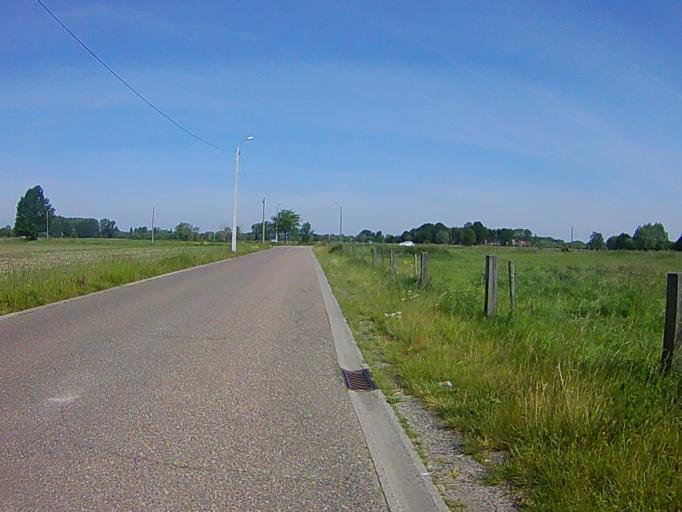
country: BE
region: Flanders
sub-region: Provincie Vlaams-Brabant
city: Londerzeel
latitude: 51.0289
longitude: 4.3157
